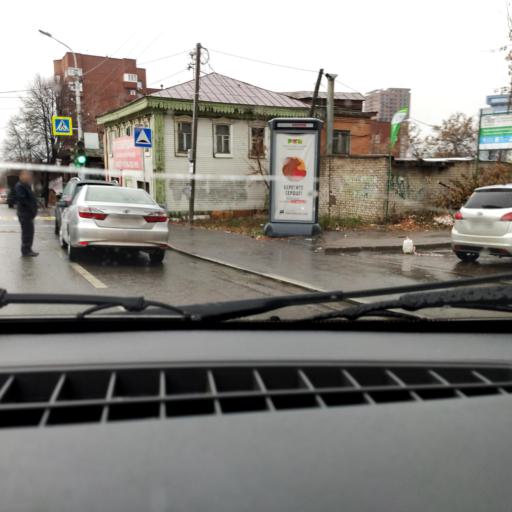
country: RU
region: Bashkortostan
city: Ufa
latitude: 54.7475
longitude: 55.9599
